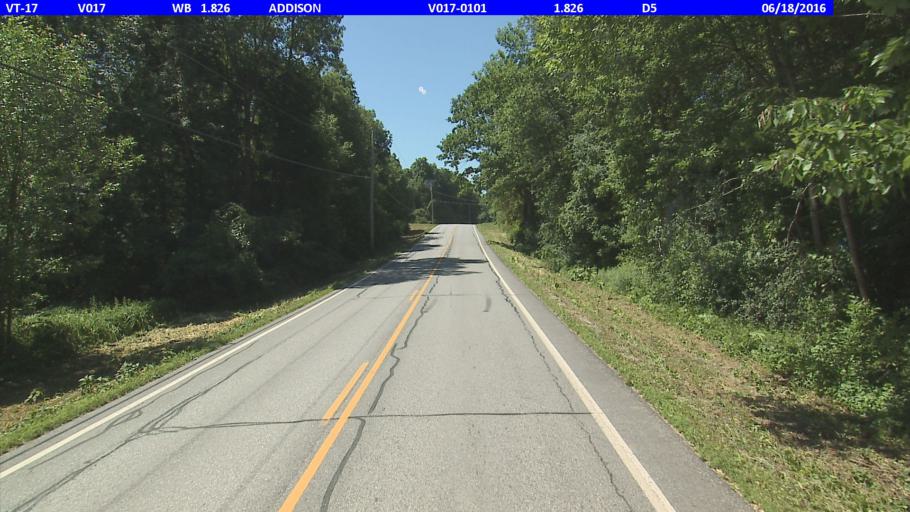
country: US
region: New York
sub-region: Essex County
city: Port Henry
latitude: 44.0559
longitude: -73.4107
